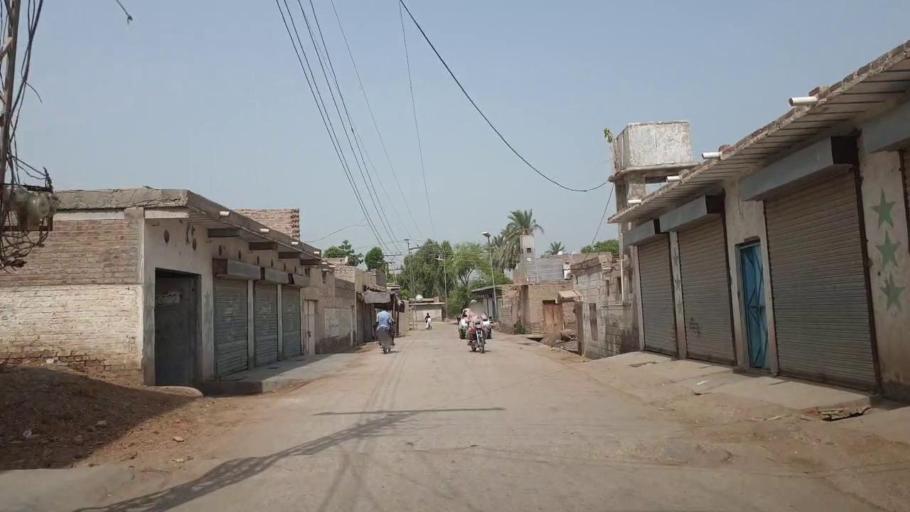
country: PK
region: Sindh
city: Gambat
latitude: 27.3779
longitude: 68.5144
